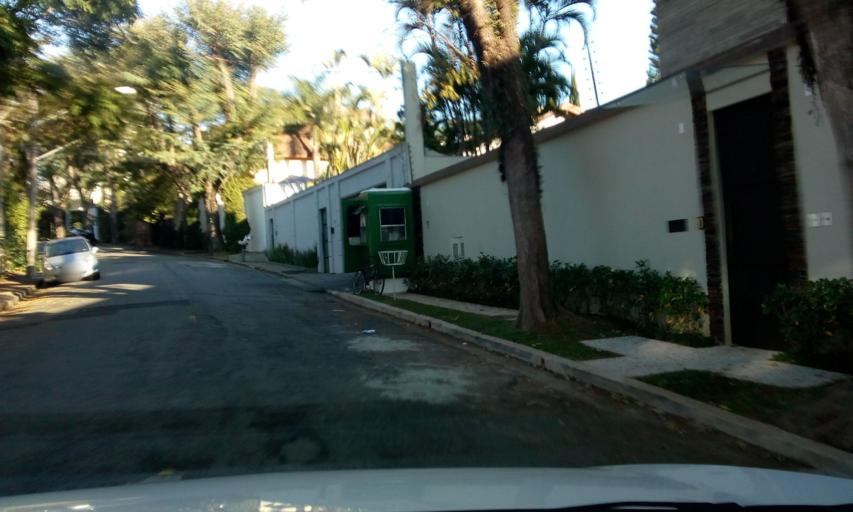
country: BR
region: Sao Paulo
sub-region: Sao Paulo
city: Sao Paulo
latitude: -23.5961
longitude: -46.7018
